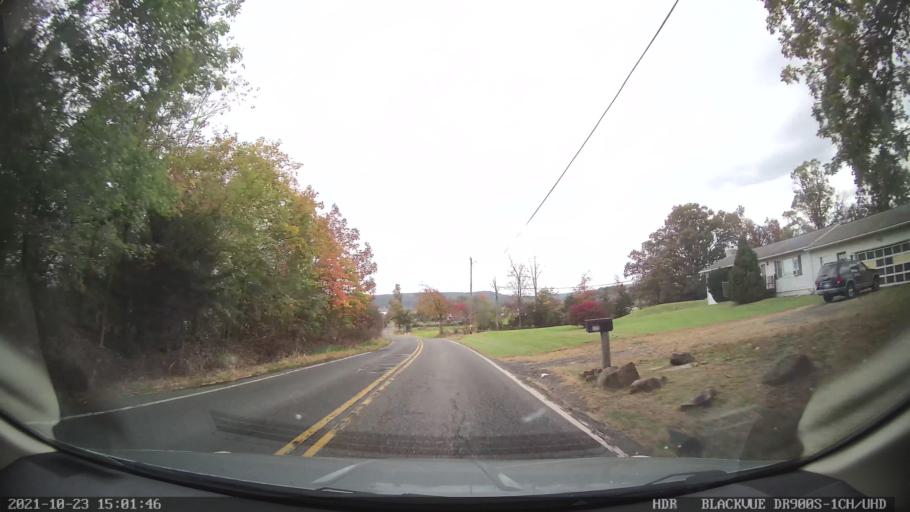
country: US
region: Pennsylvania
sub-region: Berks County
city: Bally
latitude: 40.4065
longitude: -75.5512
